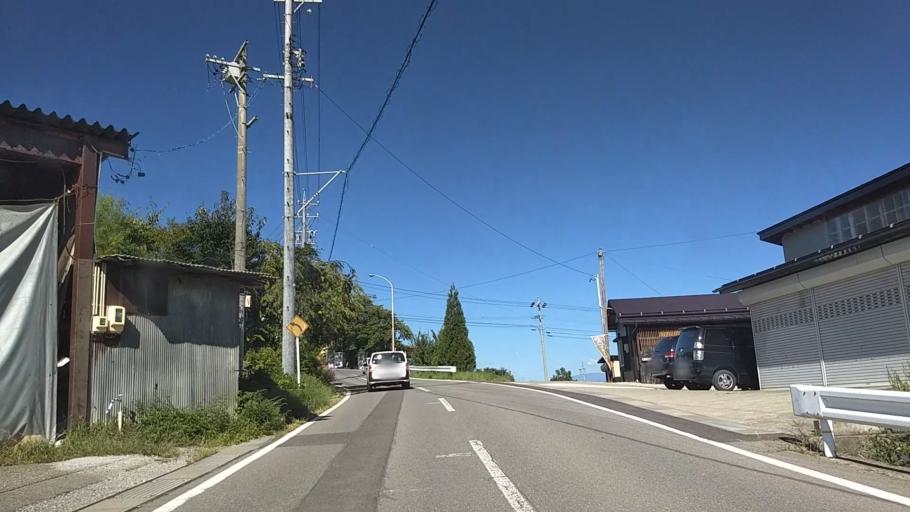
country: JP
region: Nagano
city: Nagano-shi
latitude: 36.5784
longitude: 138.1136
